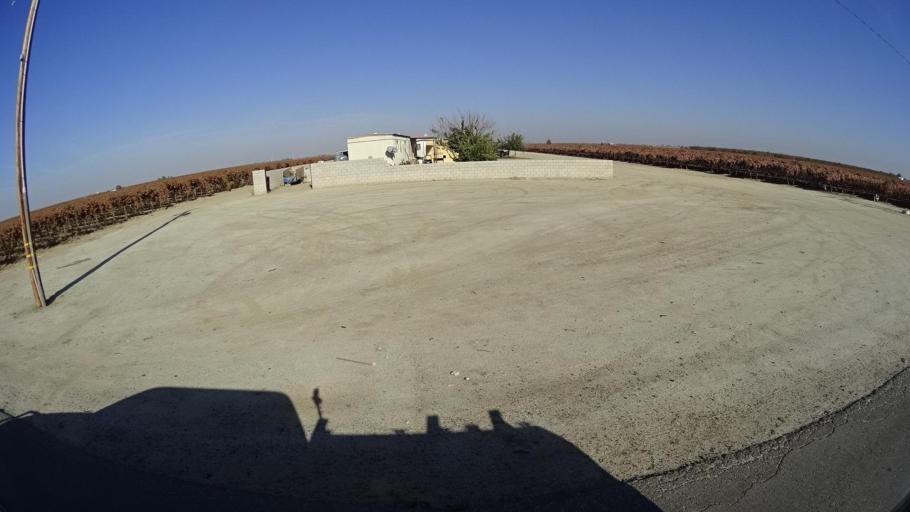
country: US
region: California
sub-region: Kern County
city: Delano
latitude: 35.7179
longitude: -119.2676
